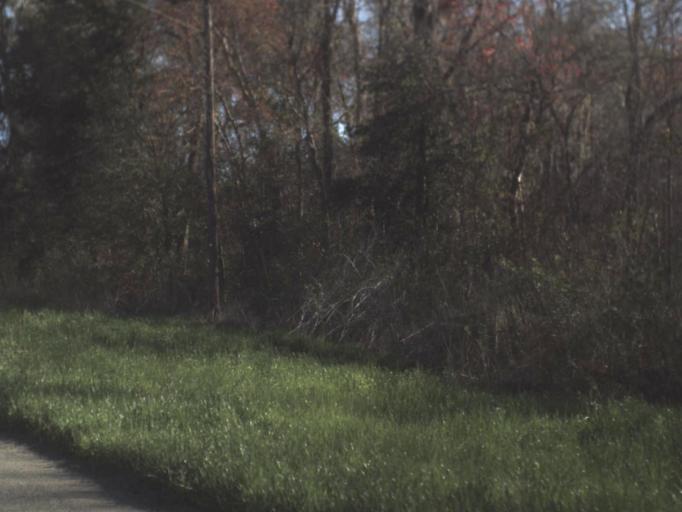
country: US
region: Georgia
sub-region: Brooks County
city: Quitman
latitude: 30.6296
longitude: -83.6459
